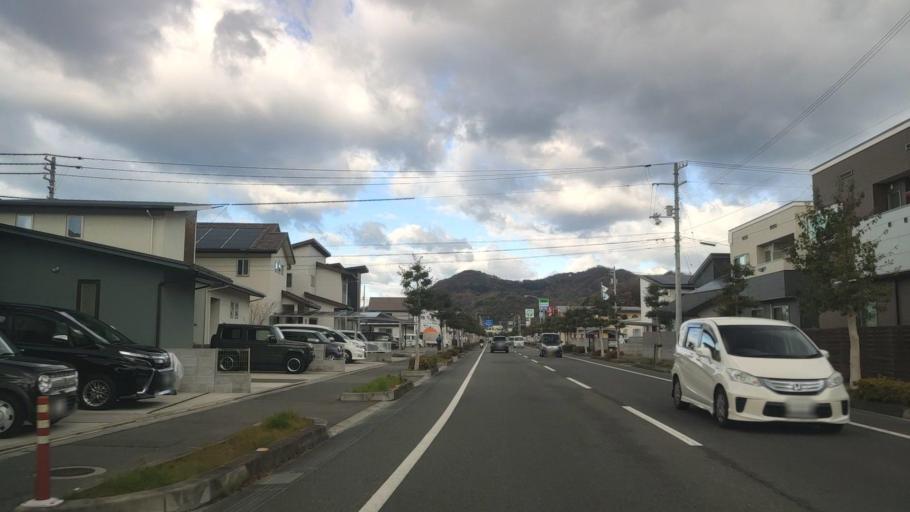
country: JP
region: Ehime
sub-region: Shikoku-chuo Shi
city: Matsuyama
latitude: 33.8688
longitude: 132.7237
